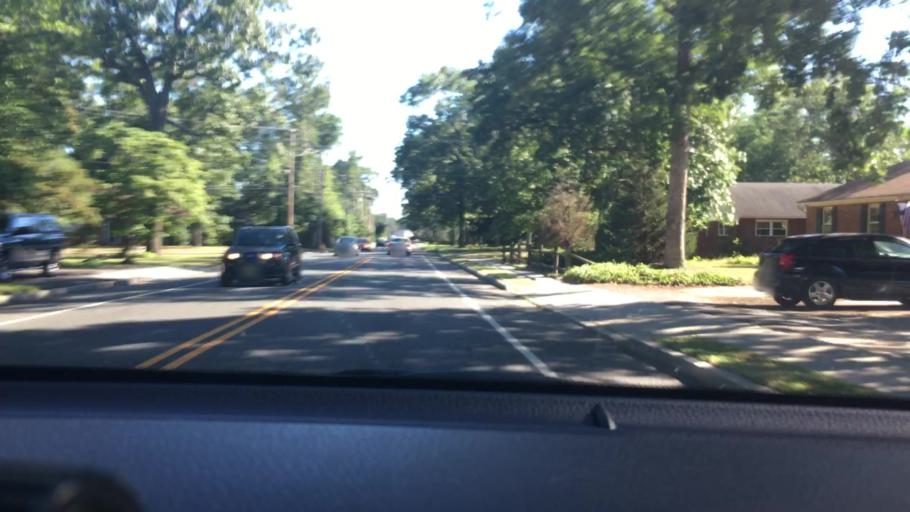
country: US
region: New Jersey
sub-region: Cumberland County
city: Millville
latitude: 39.4100
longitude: -75.0447
